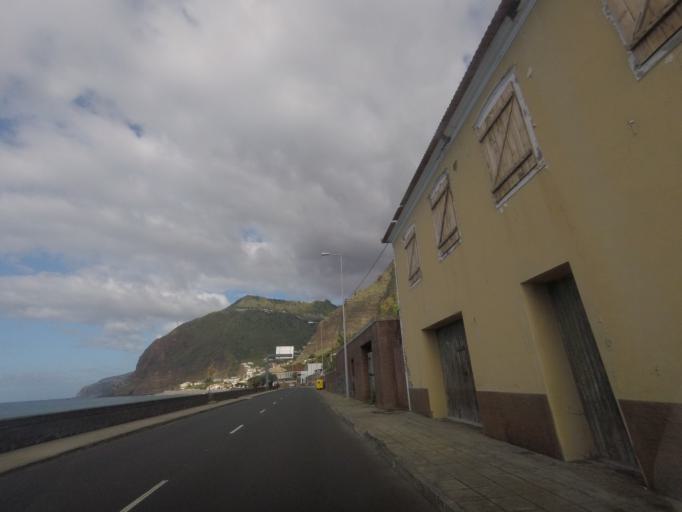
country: PT
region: Madeira
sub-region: Calheta
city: Arco da Calheta
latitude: 32.6952
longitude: -17.1275
